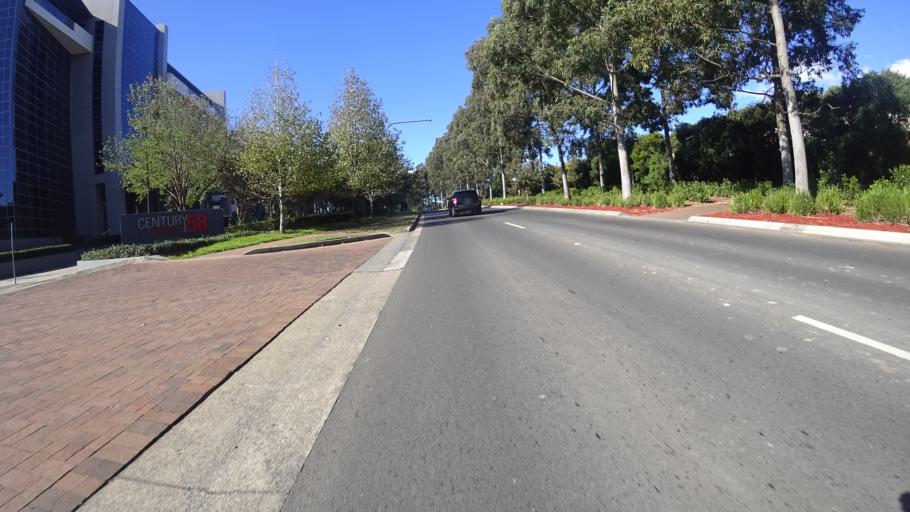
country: AU
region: New South Wales
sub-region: Blacktown
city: Stanhope Gardens
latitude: -33.7373
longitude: 150.9570
